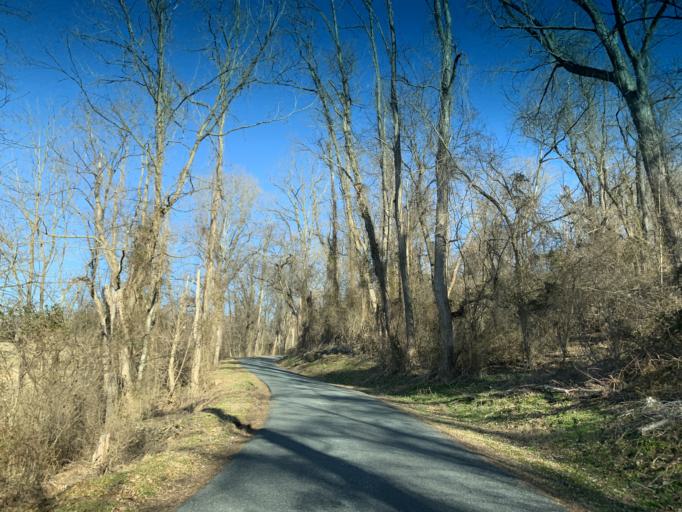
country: US
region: Maryland
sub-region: Harford County
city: South Bel Air
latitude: 39.6198
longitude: -76.2481
